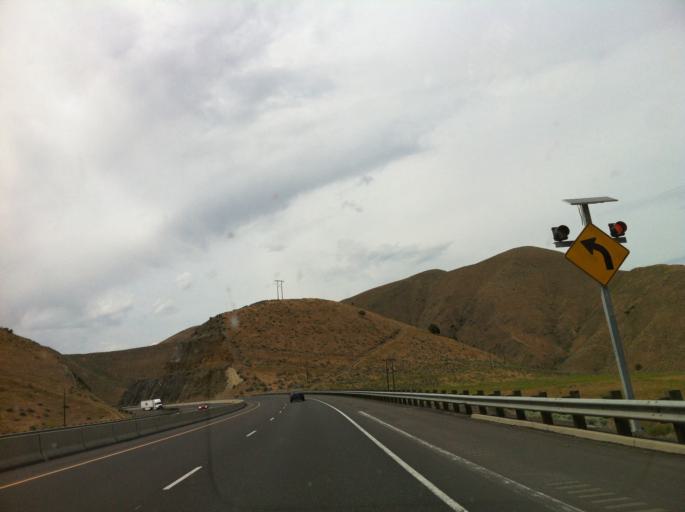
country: US
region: Idaho
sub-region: Washington County
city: Weiser
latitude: 44.4383
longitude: -117.3239
